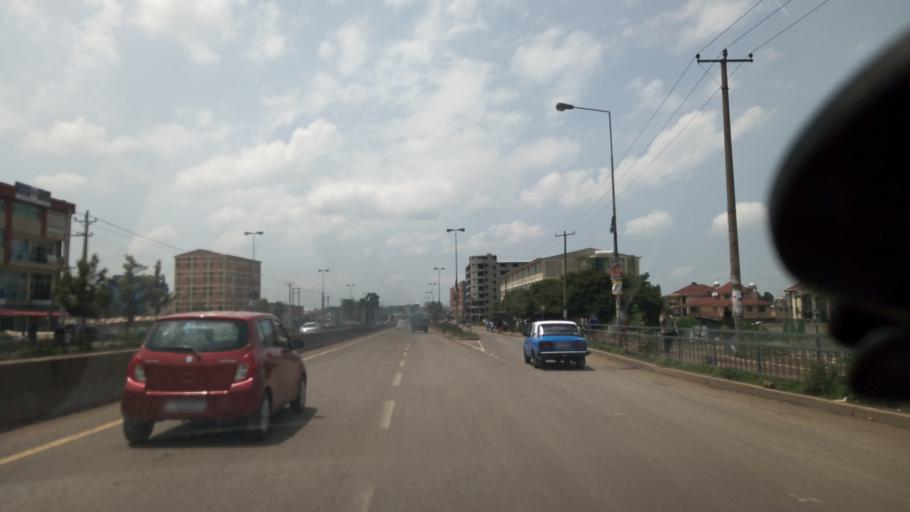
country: ET
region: Adis Abeba
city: Addis Ababa
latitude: 8.9685
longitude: 38.7225
